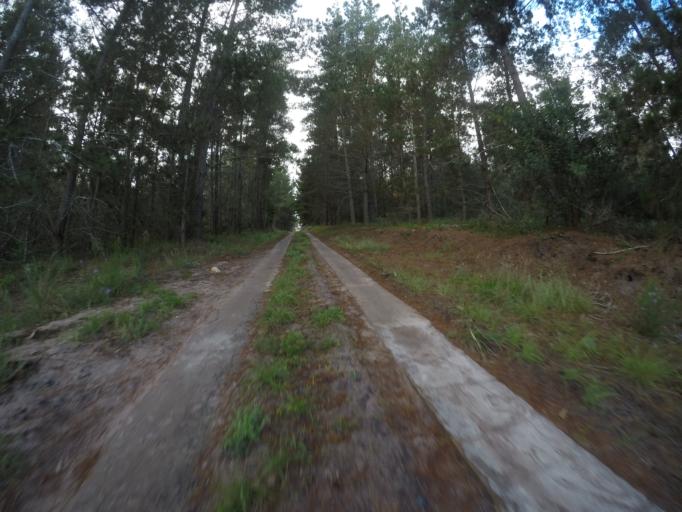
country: ZA
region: Western Cape
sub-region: Eden District Municipality
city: Knysna
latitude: -34.0099
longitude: 22.8072
